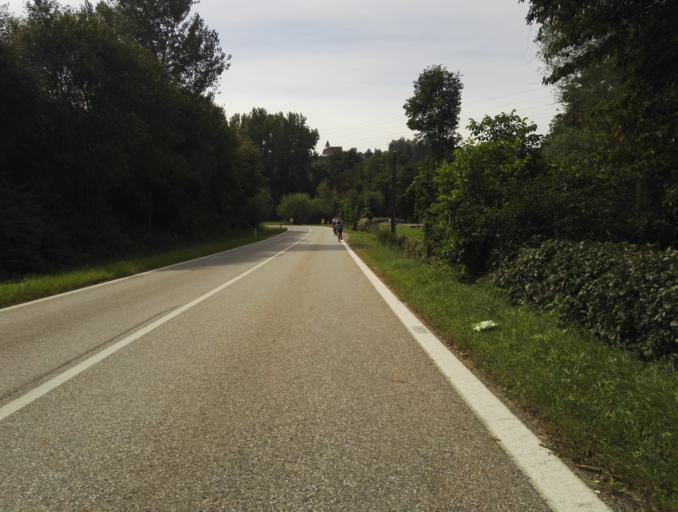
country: AT
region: Styria
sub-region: Politischer Bezirk Graz-Umgebung
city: Peggau
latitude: 47.2085
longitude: 15.3378
